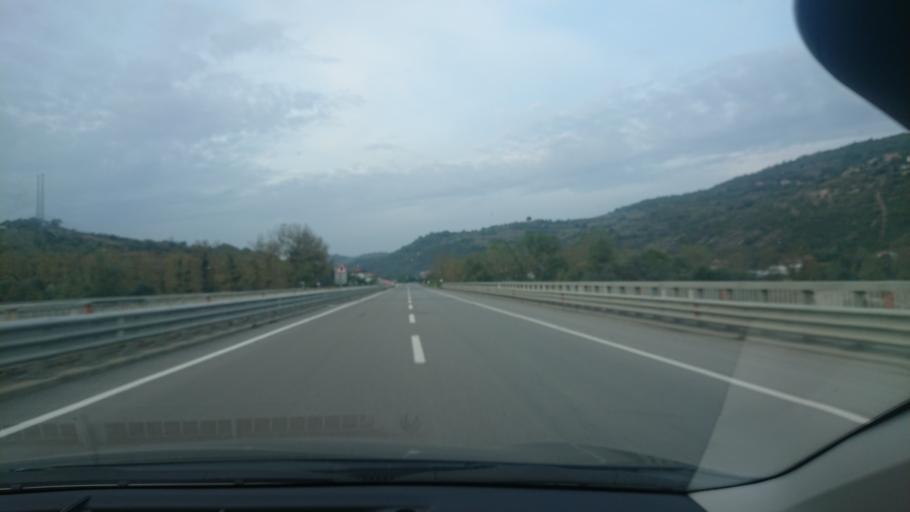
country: TR
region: Zonguldak
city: Gokcebey
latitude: 41.3366
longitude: 32.0813
